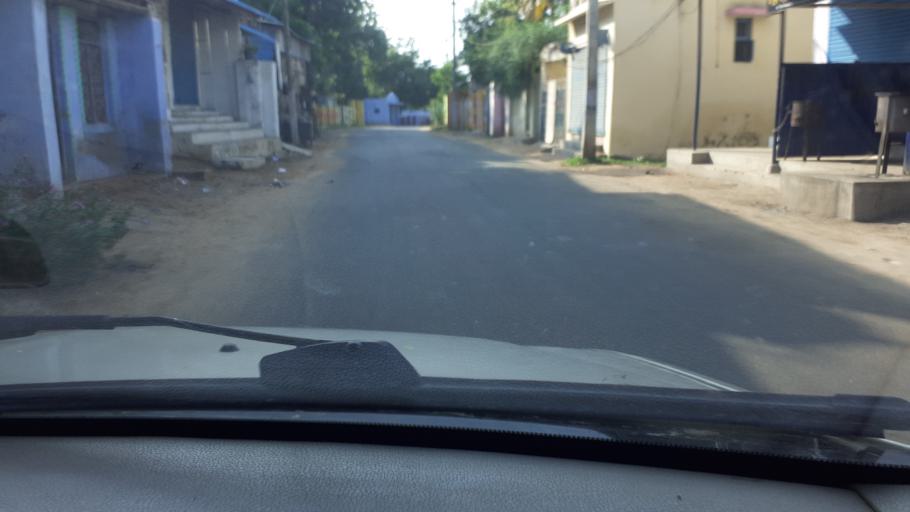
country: IN
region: Tamil Nadu
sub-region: Thoothukkudi
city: Eral
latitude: 8.5782
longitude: 78.0318
